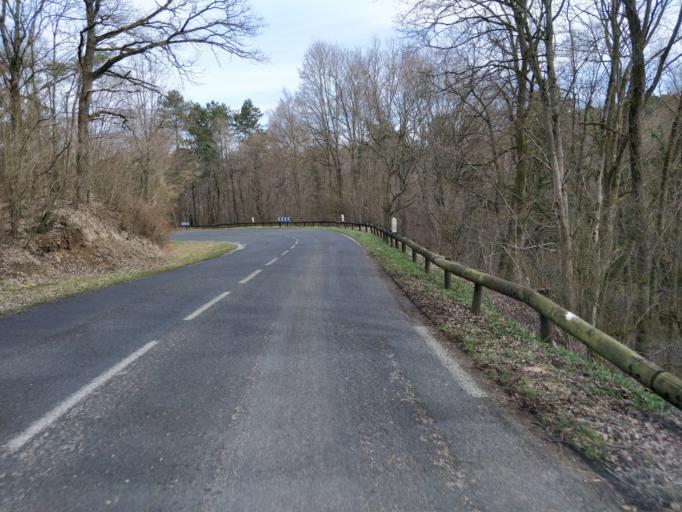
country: FR
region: Lorraine
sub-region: Departement de Meurthe-et-Moselle
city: Pagny-sur-Moselle
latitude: 48.9455
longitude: 5.8874
